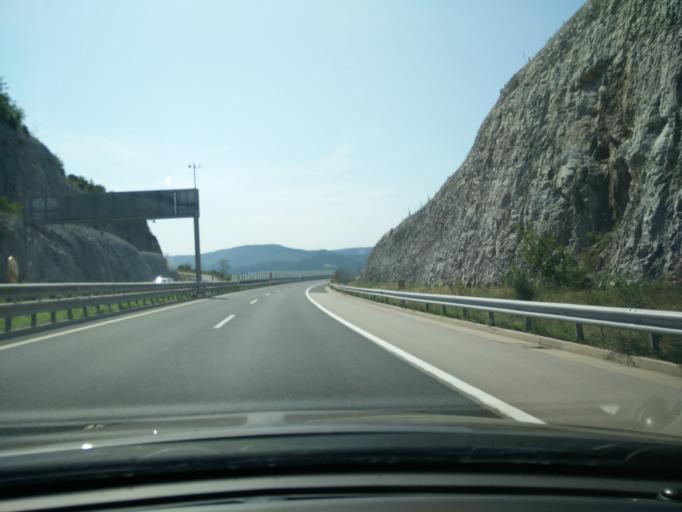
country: IT
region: Friuli Venezia Giulia
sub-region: Provincia di Trieste
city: Dolina
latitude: 45.5608
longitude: 13.8715
